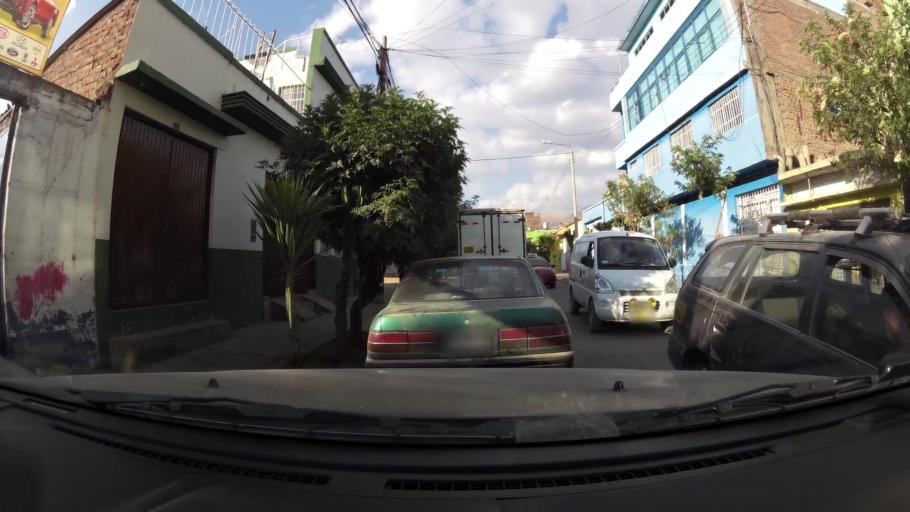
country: PE
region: Junin
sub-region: Provincia de Huancayo
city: El Tambo
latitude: -12.0529
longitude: -75.2187
